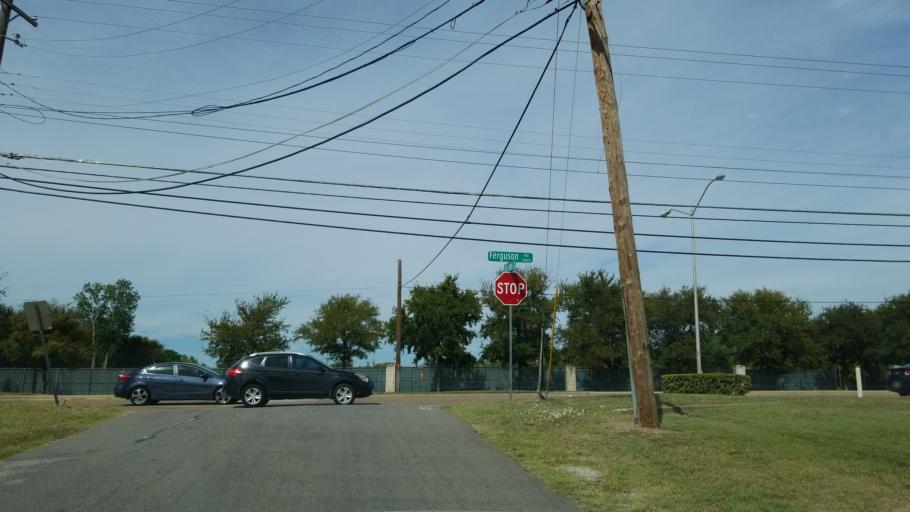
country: US
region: Texas
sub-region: Dallas County
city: Highland Park
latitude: 32.7972
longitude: -96.7190
